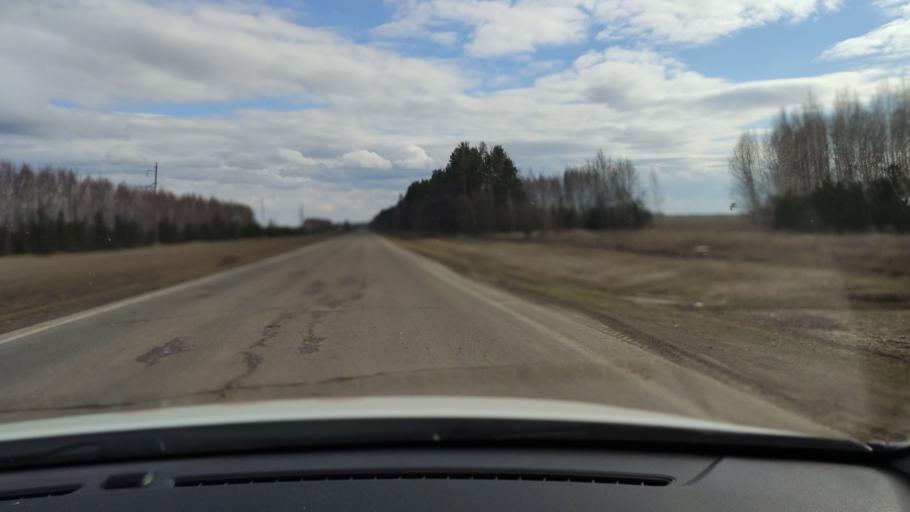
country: RU
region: Tatarstan
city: Vysokaya Gora
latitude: 56.0499
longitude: 49.2140
